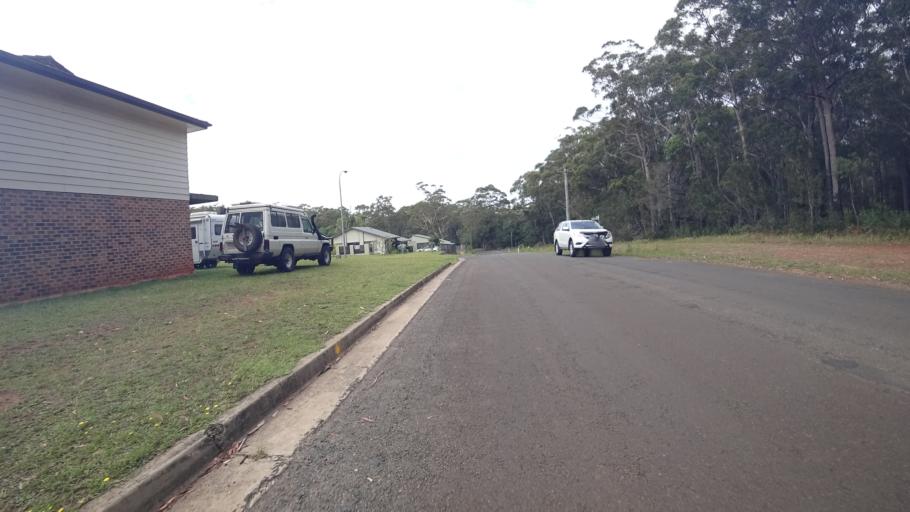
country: AU
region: New South Wales
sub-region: Shoalhaven Shire
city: Milton
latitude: -35.2586
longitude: 150.5052
